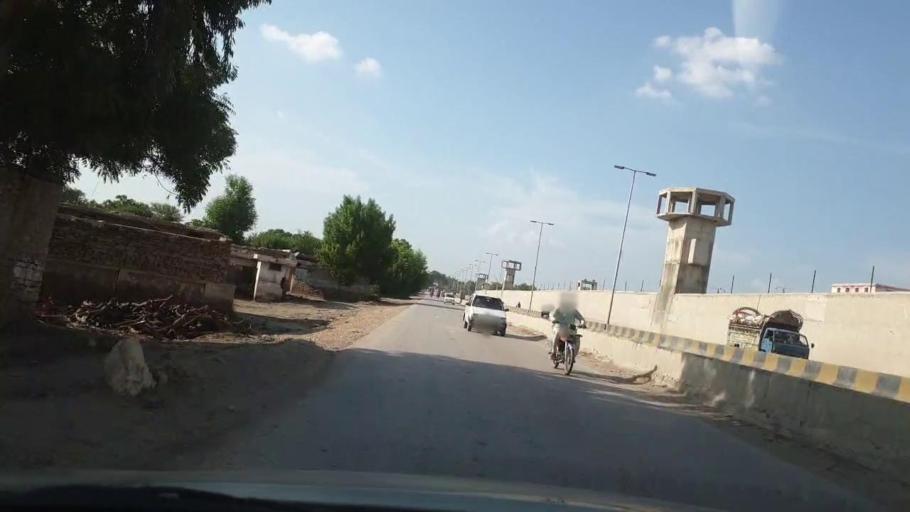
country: PK
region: Sindh
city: Sukkur
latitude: 27.6649
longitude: 68.8467
